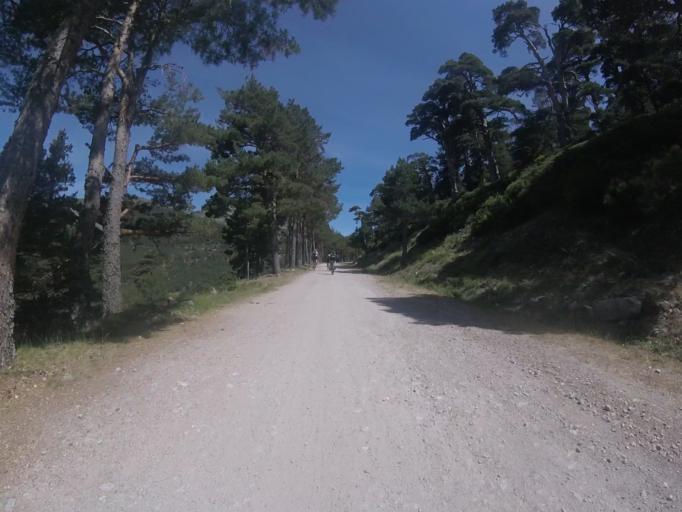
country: ES
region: Madrid
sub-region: Provincia de Madrid
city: Cercedilla
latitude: 40.7871
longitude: -4.0589
